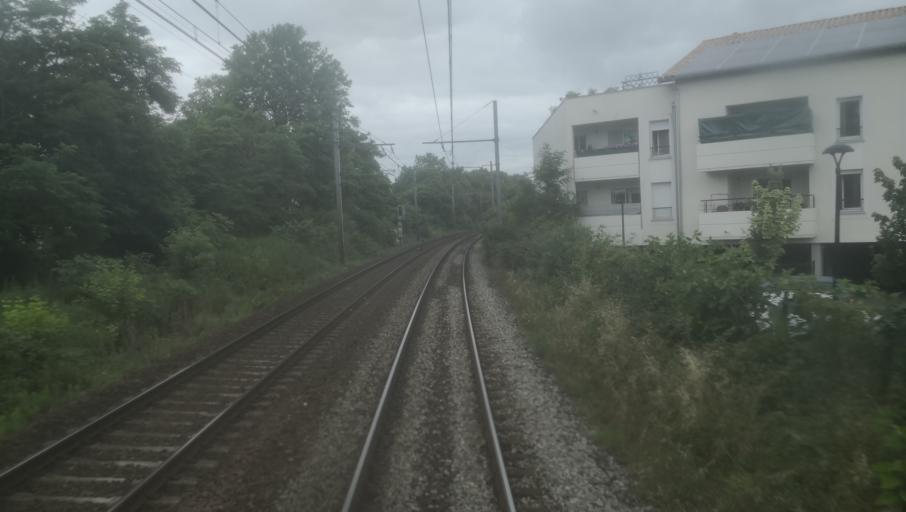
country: FR
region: Midi-Pyrenees
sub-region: Departement de la Haute-Garonne
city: Saint-Jory
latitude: 43.7421
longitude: 1.3676
